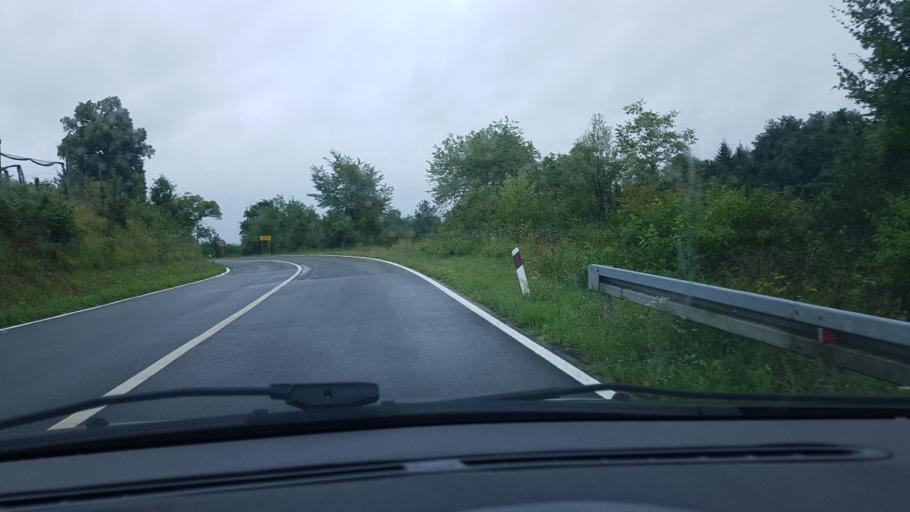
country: SI
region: Crnomelj
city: Crnomelj
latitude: 45.4475
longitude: 15.3297
